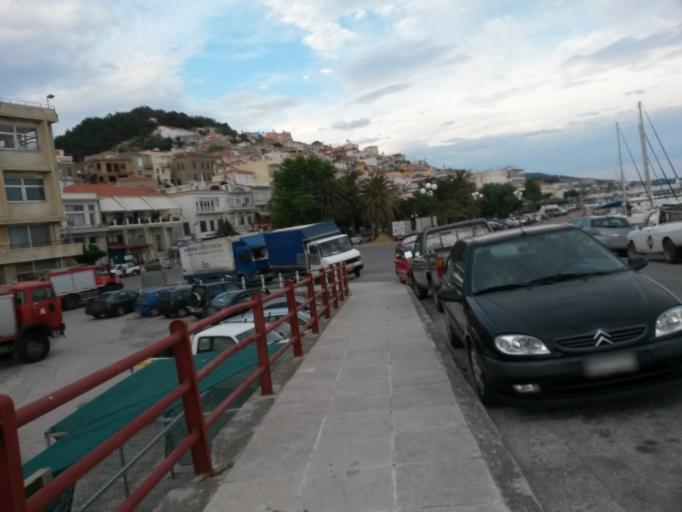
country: GR
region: North Aegean
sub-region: Nomos Lesvou
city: Plomarion
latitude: 38.9748
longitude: 26.3679
